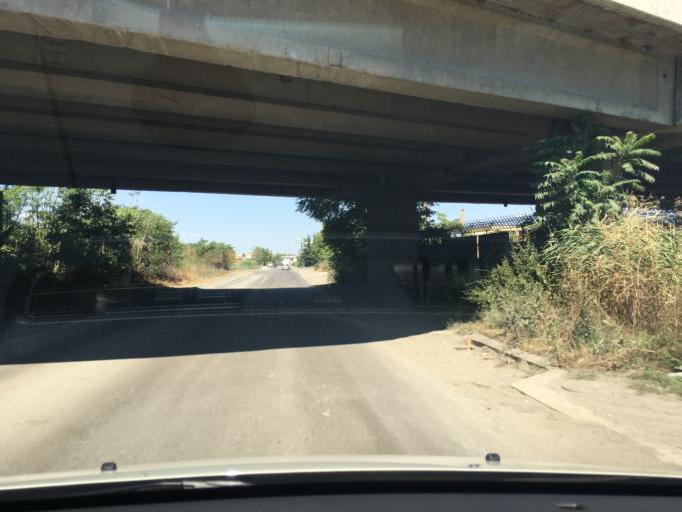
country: BG
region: Burgas
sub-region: Obshtina Burgas
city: Burgas
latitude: 42.4981
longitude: 27.4559
